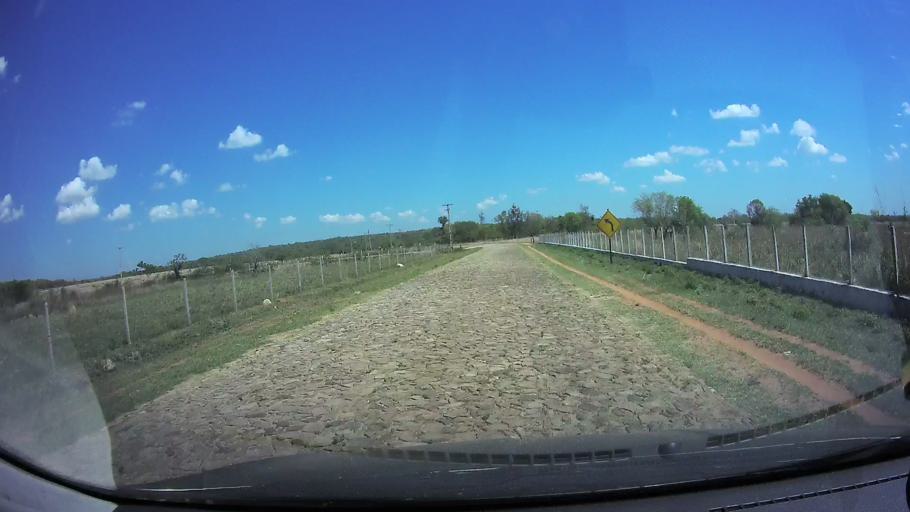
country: PY
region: Cordillera
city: Emboscada
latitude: -25.1229
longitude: -57.2746
